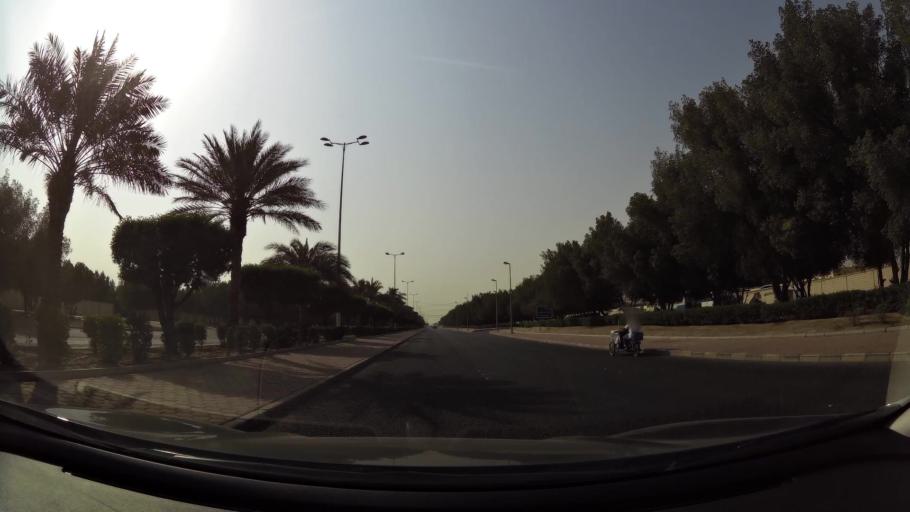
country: KW
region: Al Asimah
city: Ar Rabiyah
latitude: 29.3031
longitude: 47.8321
